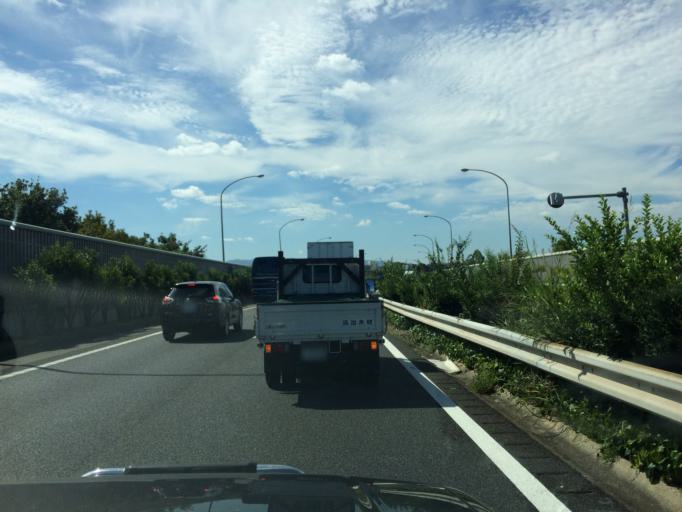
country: JP
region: Osaka
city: Takaishi
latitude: 34.5043
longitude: 135.4893
